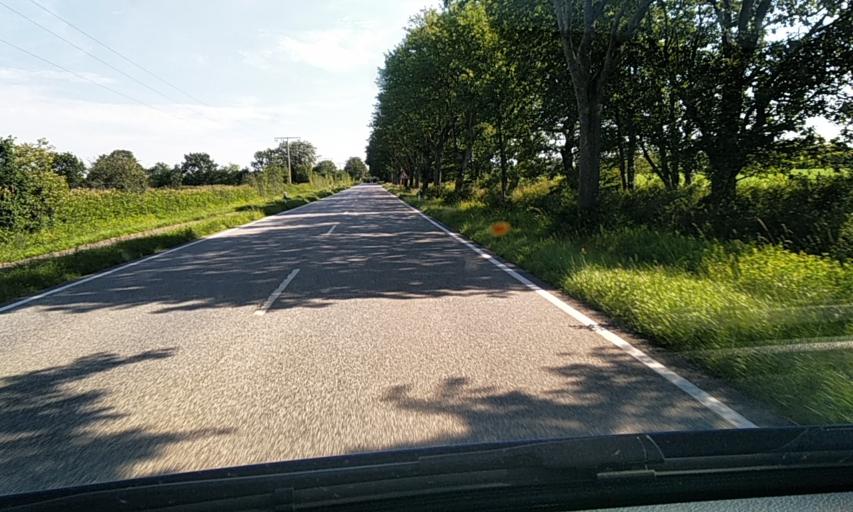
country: DE
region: Schleswig-Holstein
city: Fockbek
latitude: 54.2935
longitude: 9.5850
